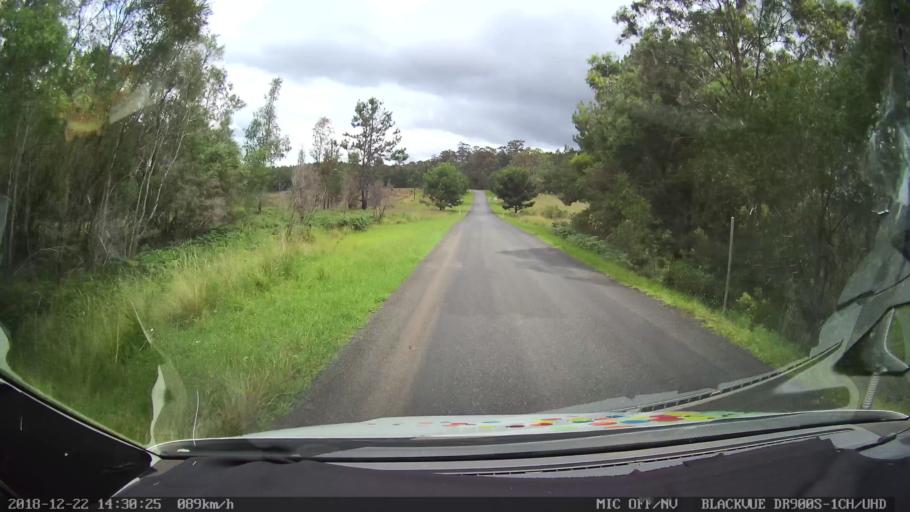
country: AU
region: New South Wales
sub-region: Bellingen
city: Dorrigo
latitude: -30.0861
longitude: 152.6316
